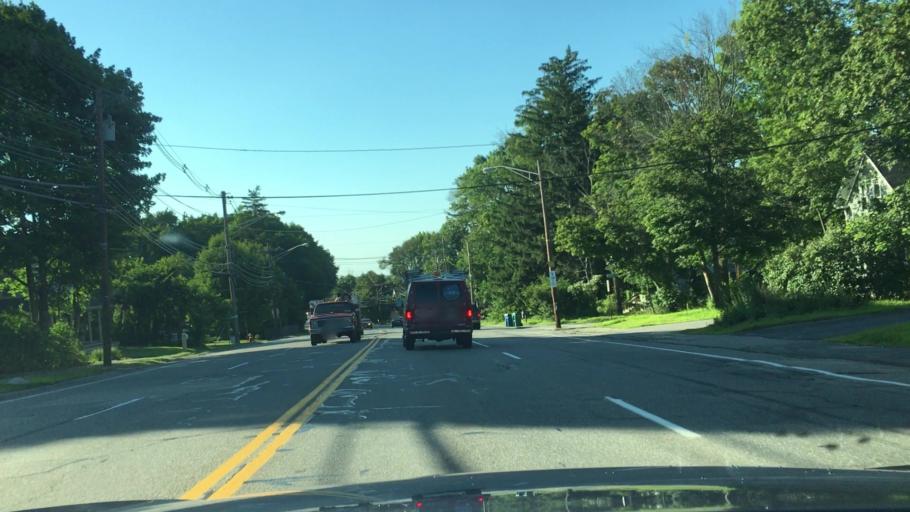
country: US
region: Massachusetts
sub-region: Middlesex County
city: Billerica
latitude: 42.5620
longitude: -71.2700
